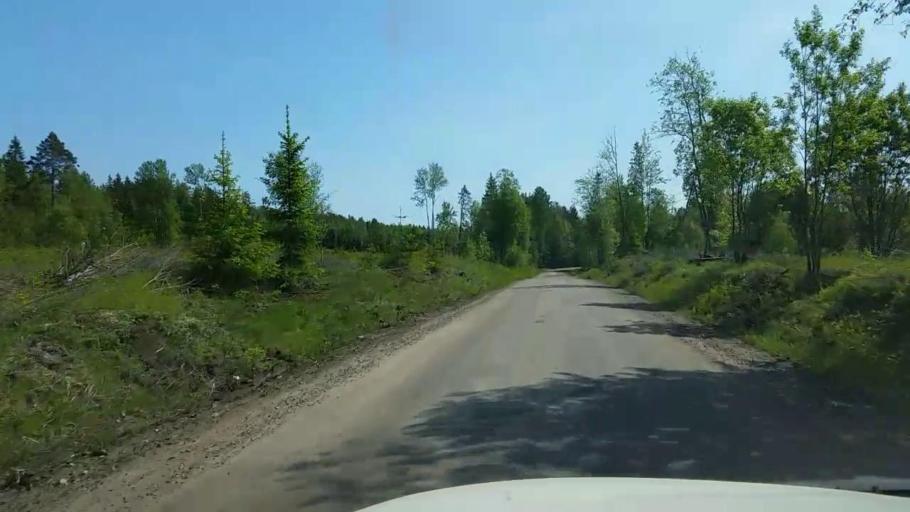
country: SE
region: Gaevleborg
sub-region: Hudiksvalls Kommun
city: Sorforsa
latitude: 61.7237
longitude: 17.0059
